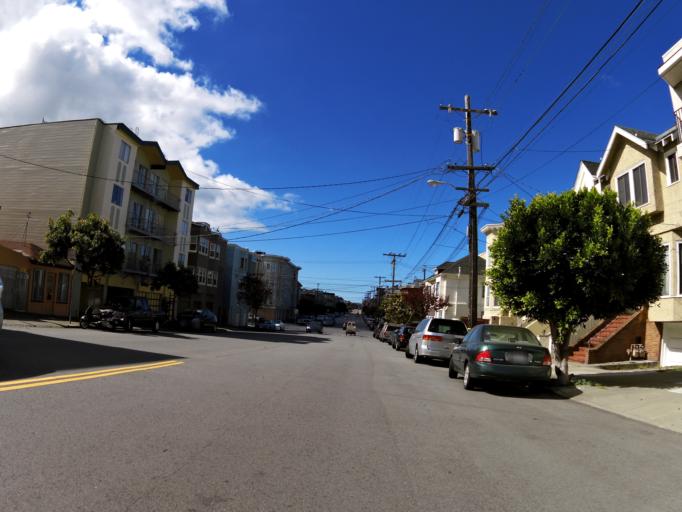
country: US
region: California
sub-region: San Francisco County
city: San Francisco
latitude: 37.7793
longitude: -122.4612
